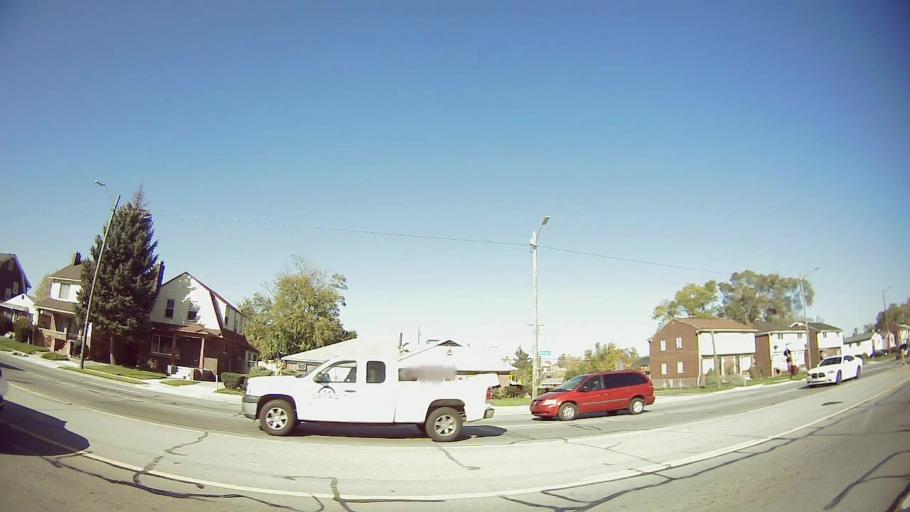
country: US
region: Michigan
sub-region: Wayne County
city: Highland Park
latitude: 42.3887
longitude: -83.1335
